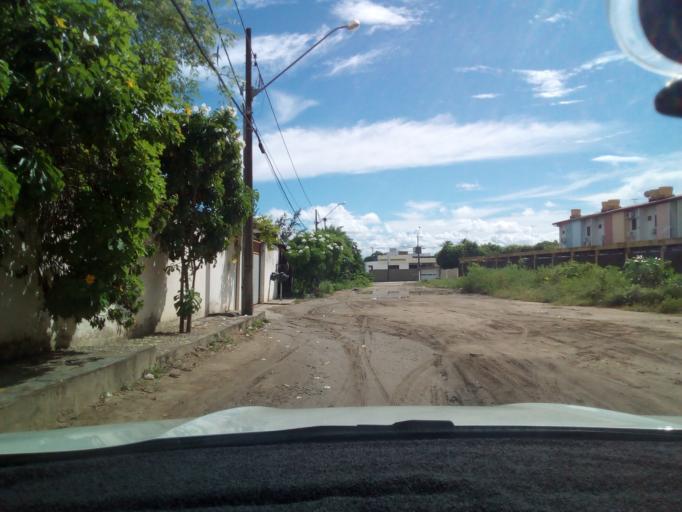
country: BR
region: Paraiba
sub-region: Joao Pessoa
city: Joao Pessoa
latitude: -7.1341
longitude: -34.8274
